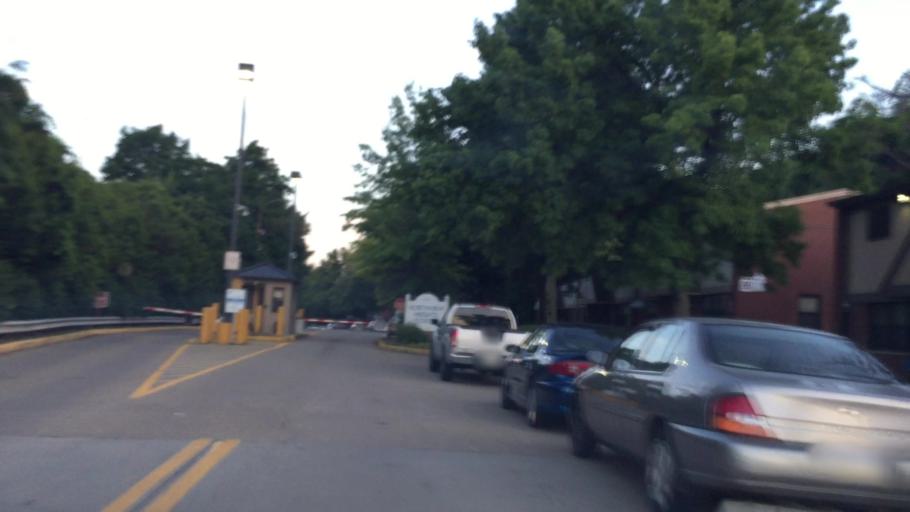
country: US
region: Pennsylvania
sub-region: Allegheny County
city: Millvale
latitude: 40.4810
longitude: -80.0022
